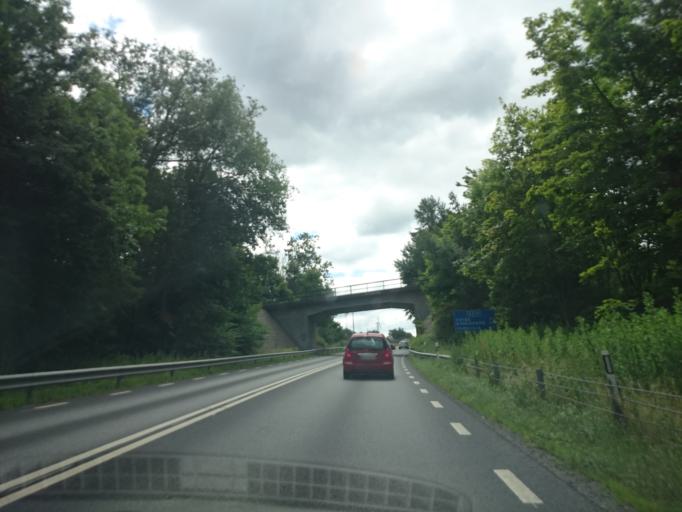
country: SE
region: Skane
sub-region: Kristianstads Kommun
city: Degeberga
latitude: 55.8013
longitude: 14.1486
